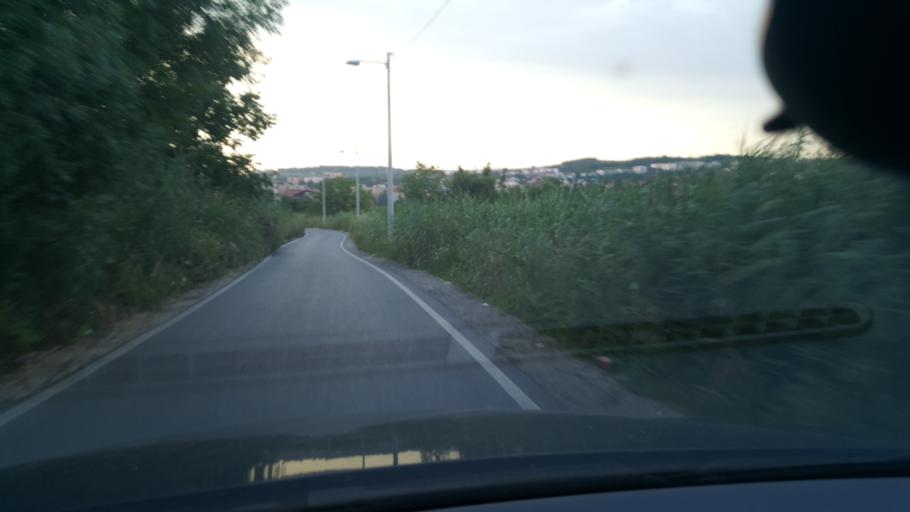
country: RS
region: Central Serbia
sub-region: Belgrade
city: Zvezdara
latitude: 44.7824
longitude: 20.5323
